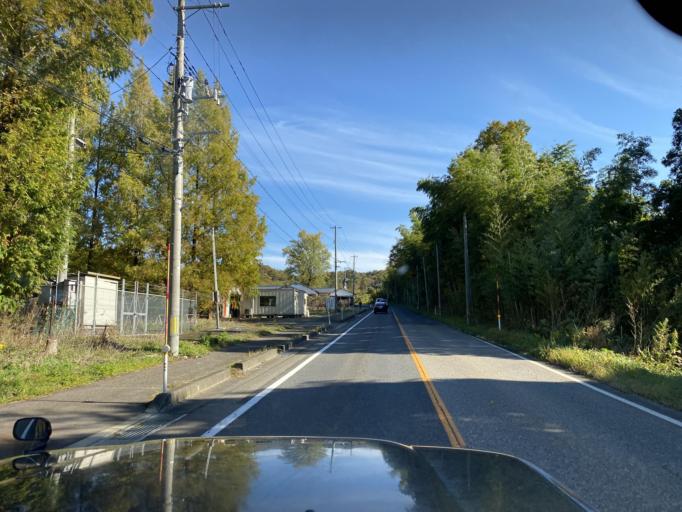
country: JP
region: Niigata
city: Niitsu-honcho
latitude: 37.7508
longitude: 139.1032
